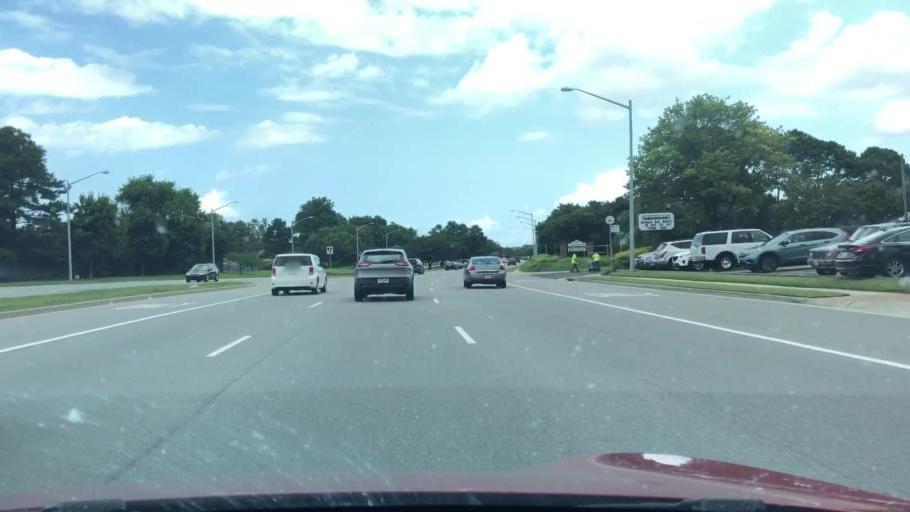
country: US
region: Virginia
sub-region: City of Chesapeake
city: Chesapeake
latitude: 36.8515
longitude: -76.1365
